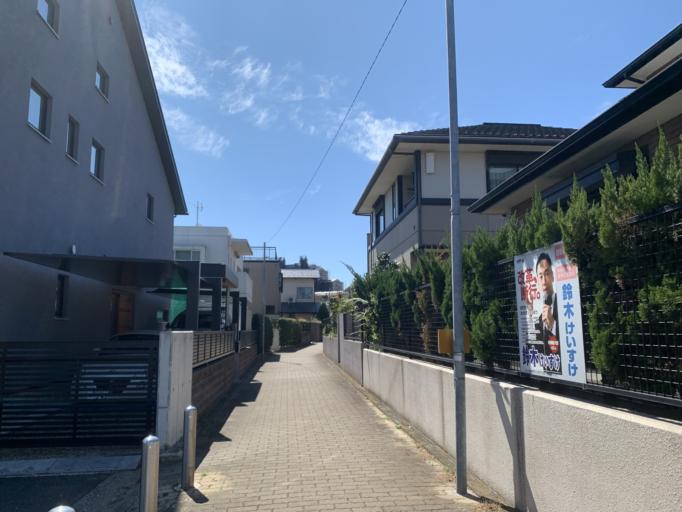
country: JP
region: Tokyo
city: Chofugaoka
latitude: 35.5536
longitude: 139.5845
